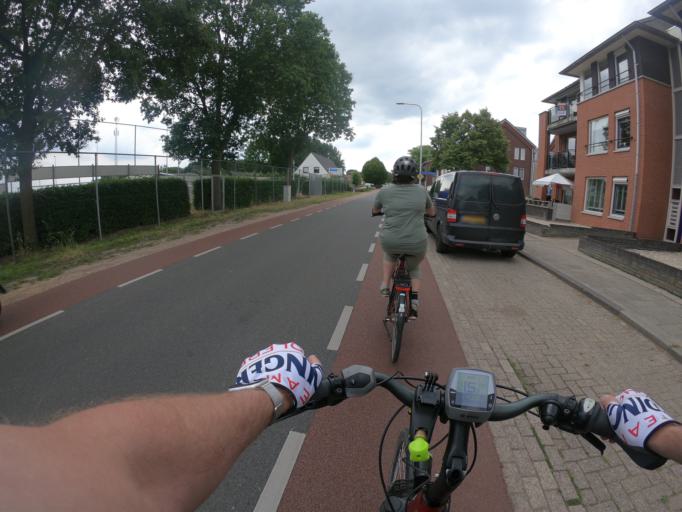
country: NL
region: Gelderland
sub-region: Gemeente Groesbeek
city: Bredeweg
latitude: 51.7572
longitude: 5.9413
